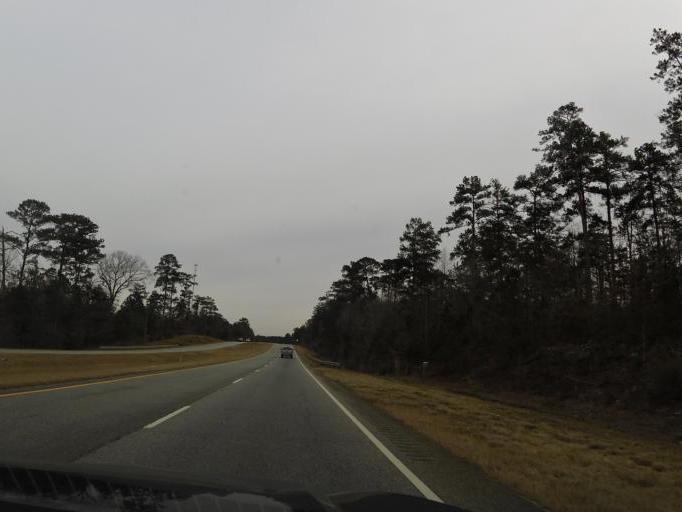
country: US
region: Georgia
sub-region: Decatur County
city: Bainbridge
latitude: 30.8808
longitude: -84.4562
